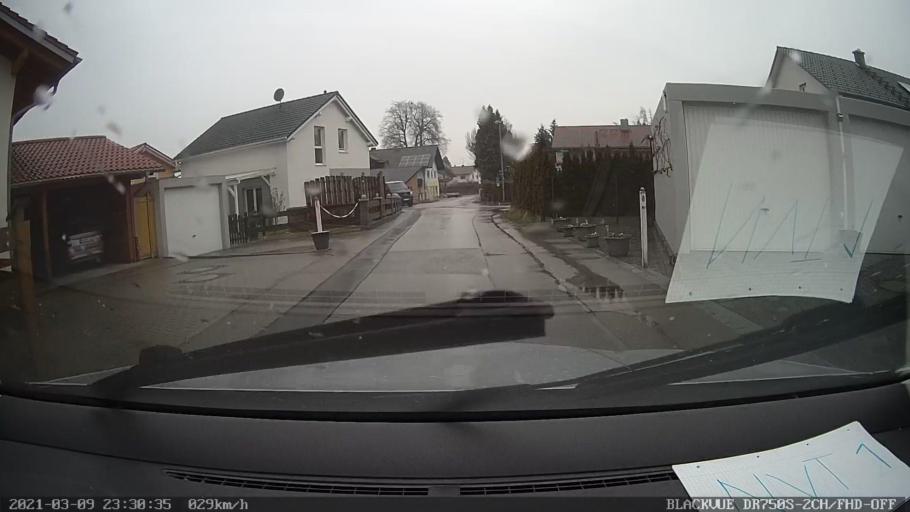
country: DE
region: Bavaria
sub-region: Upper Bavaria
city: Schonstett
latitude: 47.9802
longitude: 12.2429
